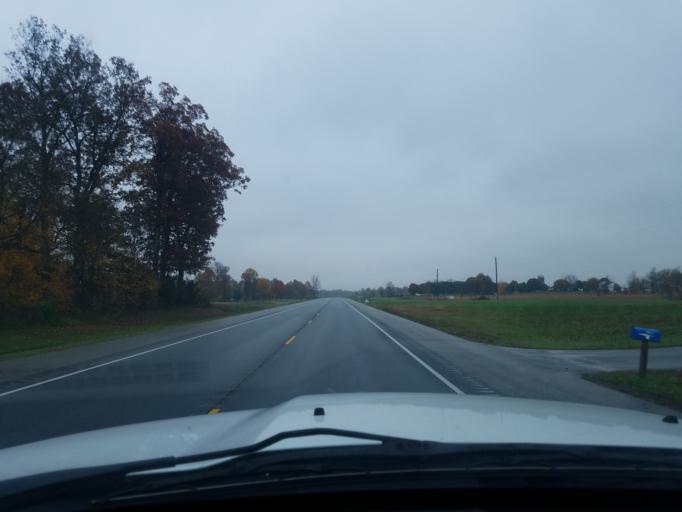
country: US
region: Kentucky
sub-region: Larue County
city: Hodgenville
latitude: 37.5054
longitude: -85.6261
